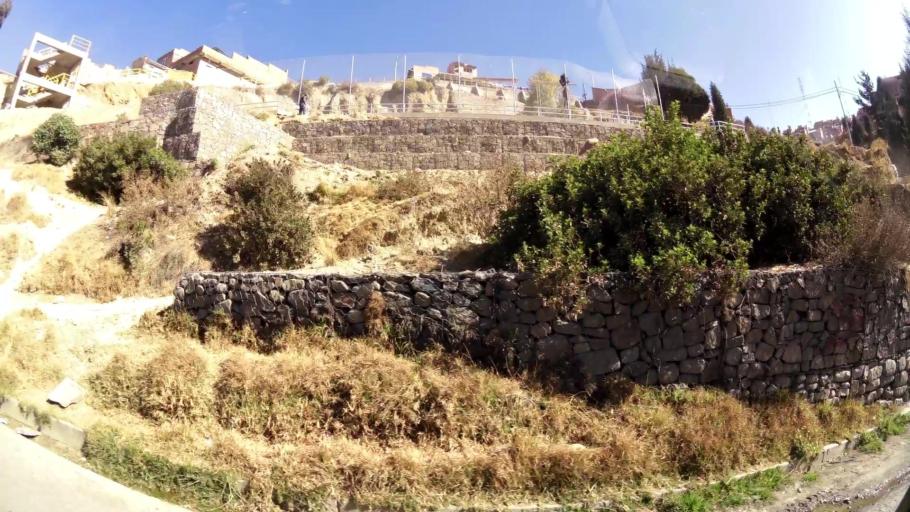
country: BO
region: La Paz
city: La Paz
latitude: -16.5209
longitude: -68.1429
